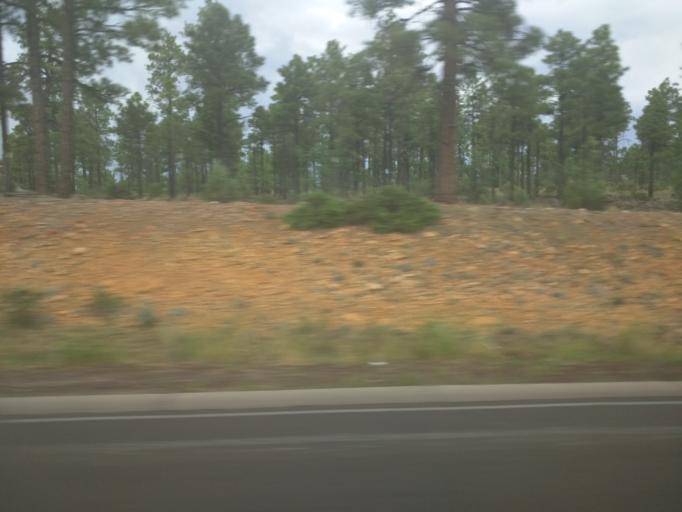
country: US
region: Arizona
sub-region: Navajo County
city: Show Low
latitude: 34.2327
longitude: -110.0302
